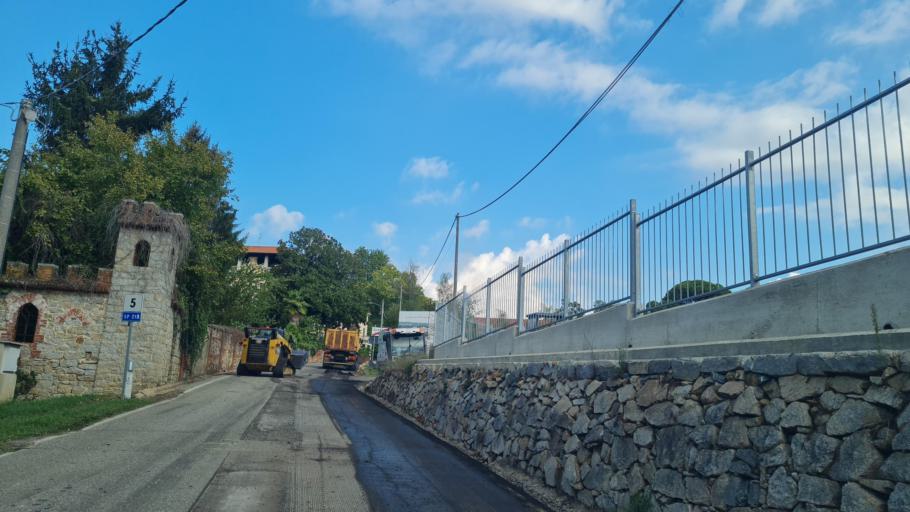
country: IT
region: Piedmont
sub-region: Provincia di Biella
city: Quaregna
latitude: 45.5841
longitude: 8.1635
